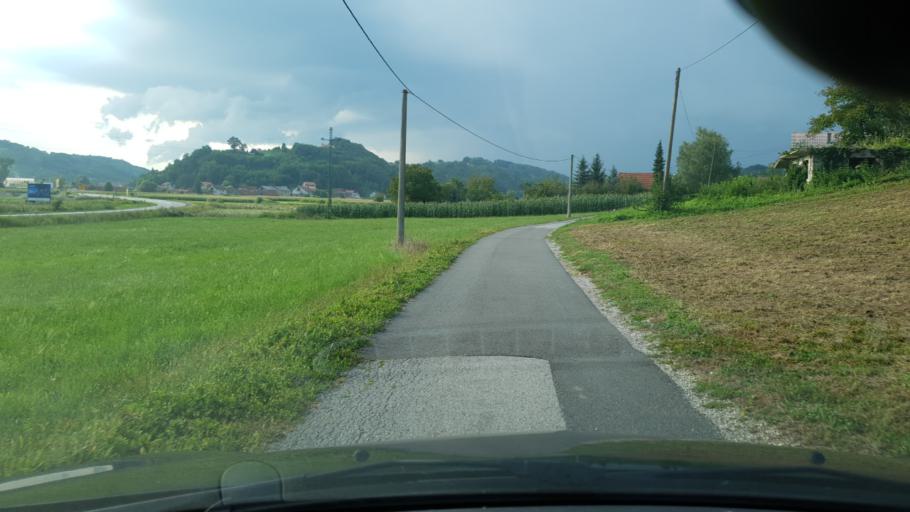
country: HR
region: Krapinsko-Zagorska
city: Zabok
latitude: 46.0935
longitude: 15.9108
